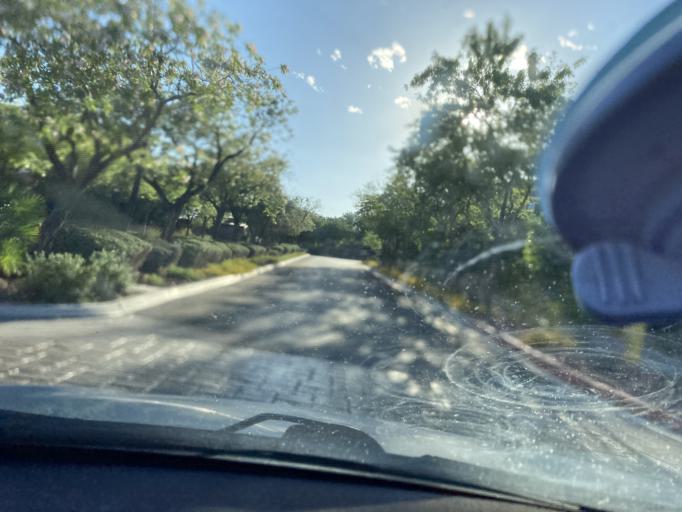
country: US
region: Nevada
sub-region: Clark County
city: Summerlin South
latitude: 36.1577
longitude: -115.3458
